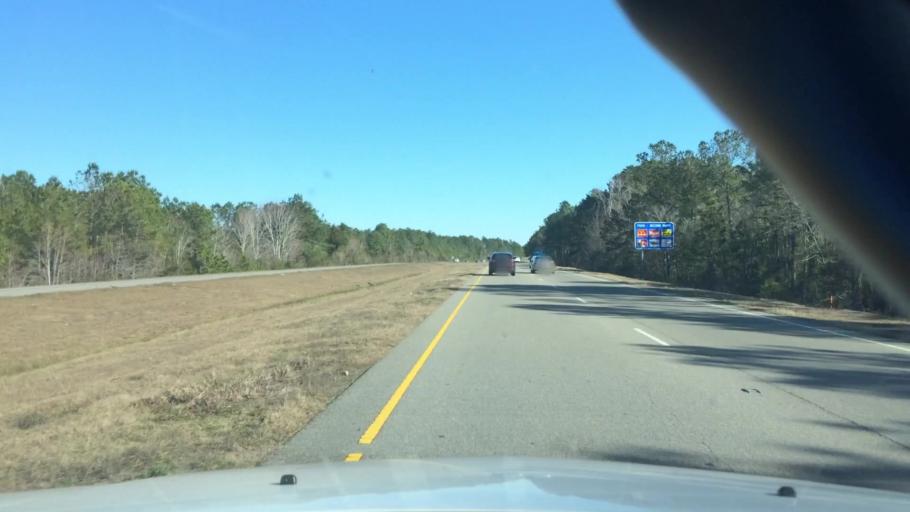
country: US
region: North Carolina
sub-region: Brunswick County
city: Shallotte
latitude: 33.9674
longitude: -78.4131
